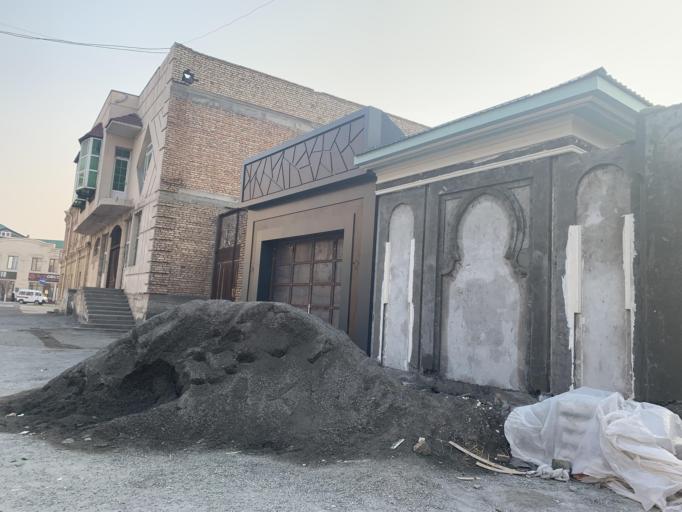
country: UZ
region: Fergana
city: Qo`qon
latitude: 40.5373
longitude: 70.9321
